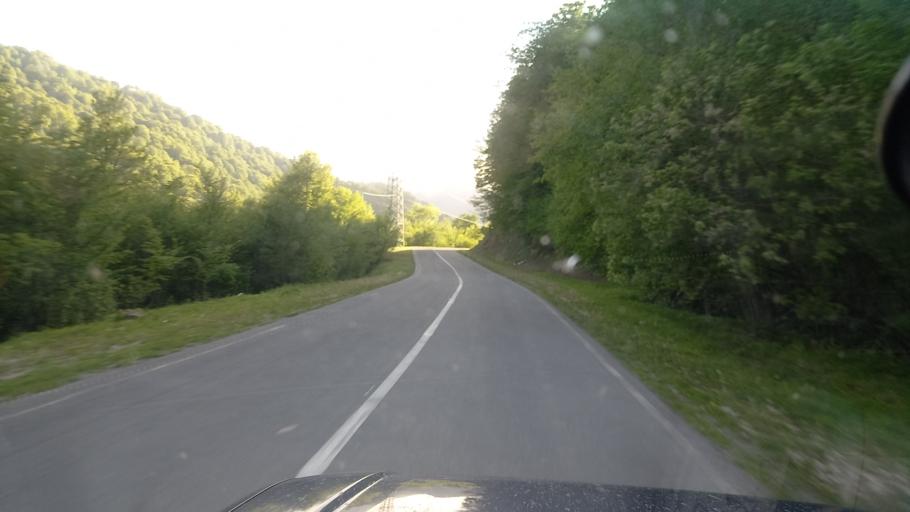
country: RU
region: Ingushetiya
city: Galashki
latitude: 42.9071
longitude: 44.9779
